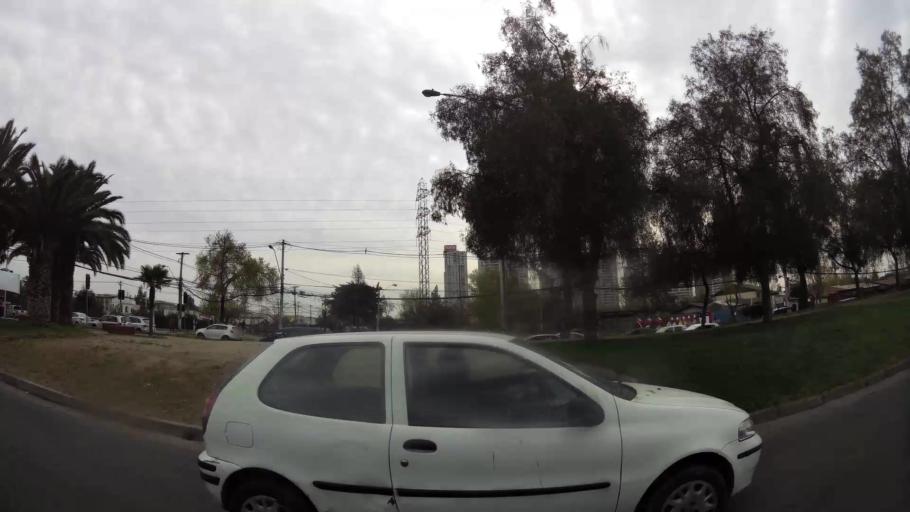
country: CL
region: Santiago Metropolitan
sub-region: Provincia de Santiago
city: Villa Presidente Frei, Nunoa, Santiago, Chile
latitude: -33.4905
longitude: -70.6116
